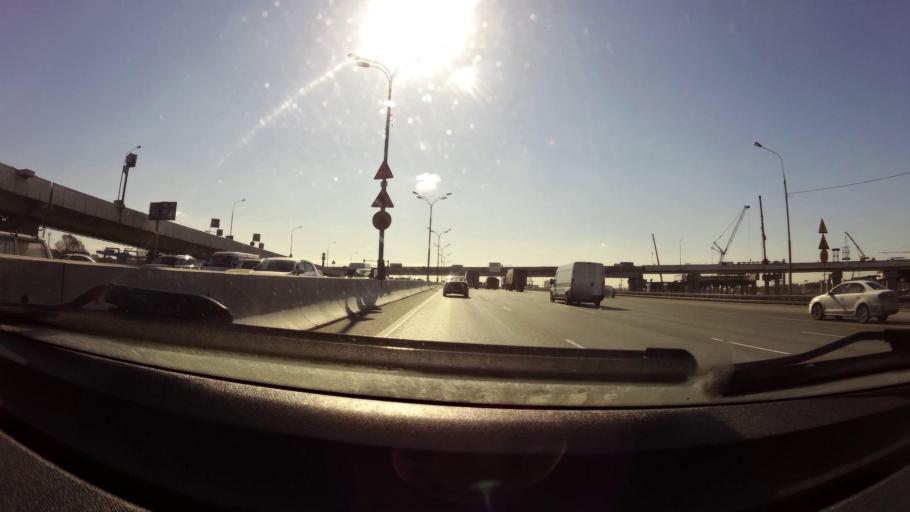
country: RU
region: Moskovskaya
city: Nemchinovka
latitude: 55.7308
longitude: 37.3771
